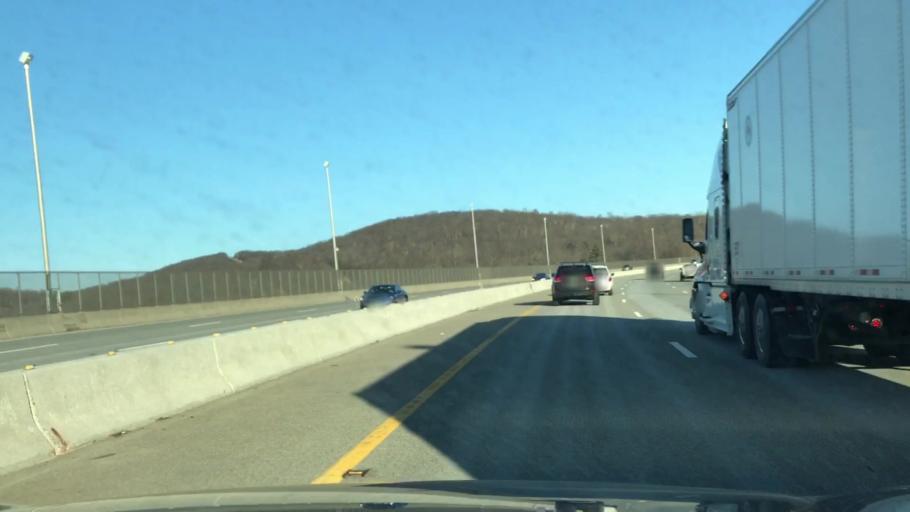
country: US
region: New Jersey
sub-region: Passaic County
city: Wanaque
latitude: 41.0262
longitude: -74.2866
